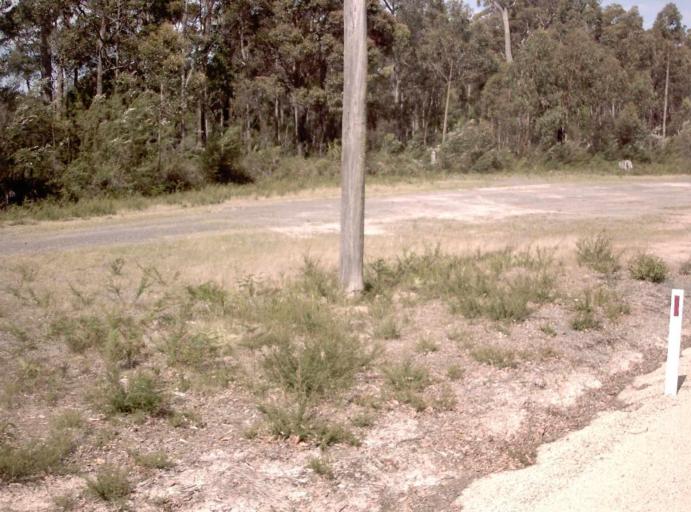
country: AU
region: New South Wales
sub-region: Bega Valley
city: Eden
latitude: -37.5469
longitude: 149.7232
